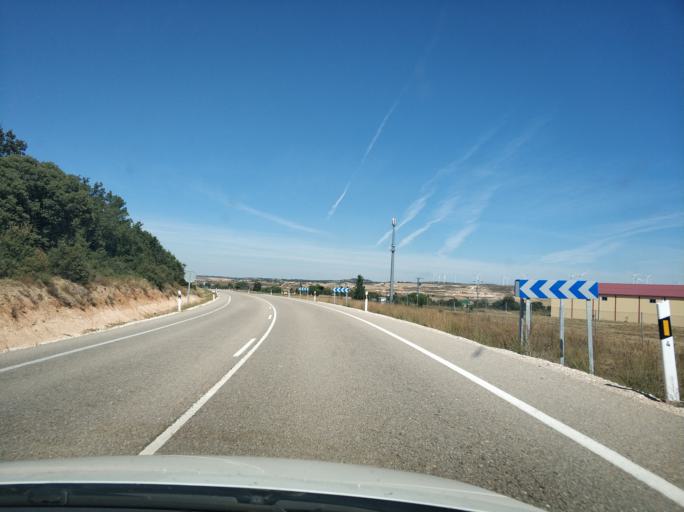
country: ES
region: Castille and Leon
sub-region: Provincia de Burgos
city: Revillarruz
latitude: 42.2190
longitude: -3.6528
